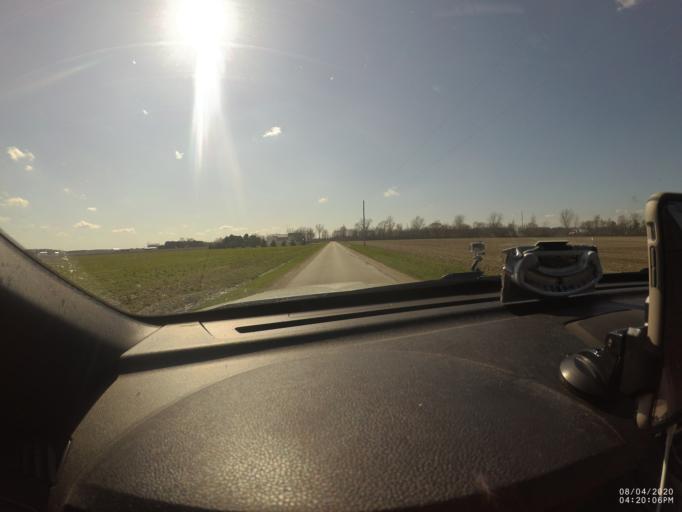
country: US
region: Ohio
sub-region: Sandusky County
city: Stony Prairie
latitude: 41.2902
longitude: -83.2101
